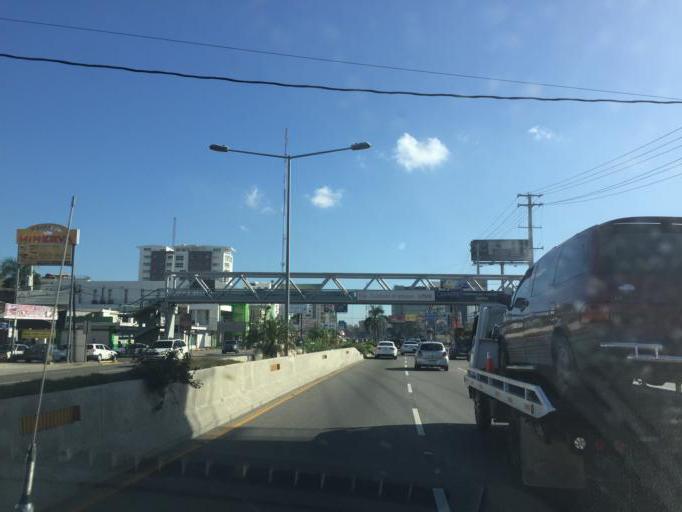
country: DO
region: Nacional
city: Bella Vista
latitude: 18.4583
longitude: -69.9461
